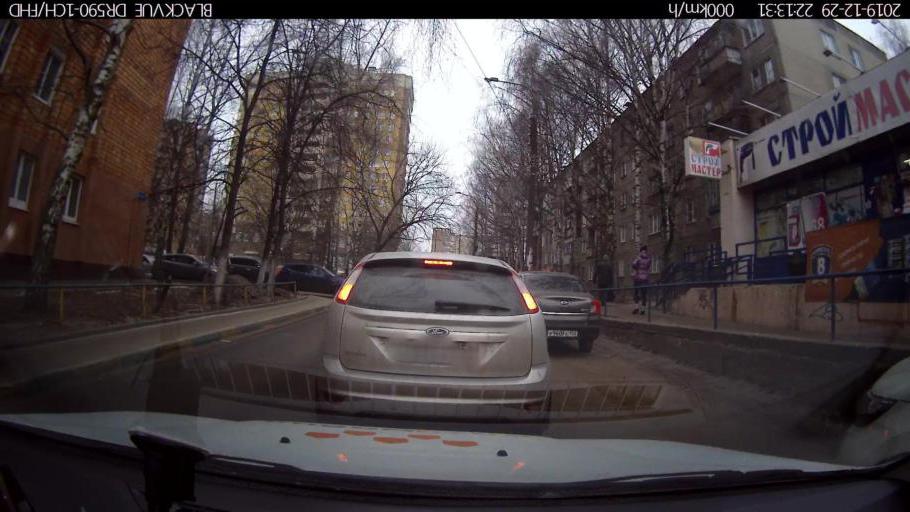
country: RU
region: Nizjnij Novgorod
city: Nizhniy Novgorod
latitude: 56.2322
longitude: 43.9530
